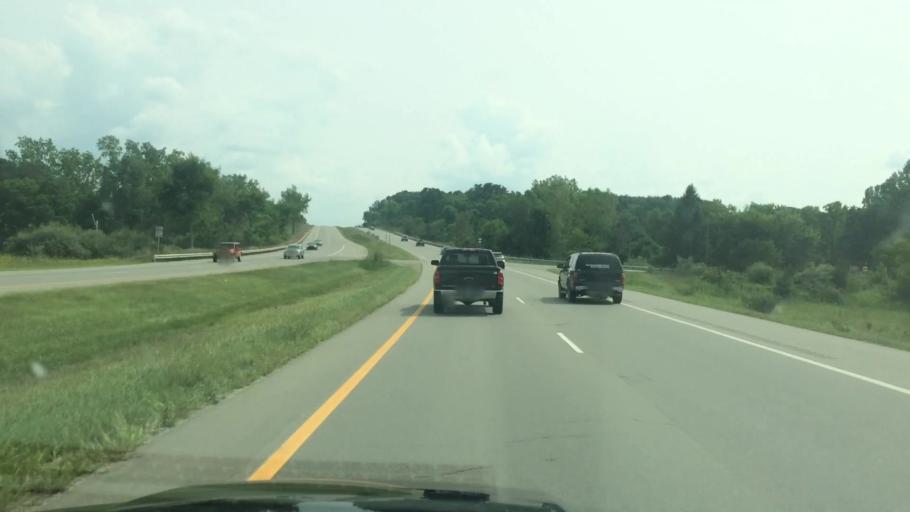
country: US
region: Michigan
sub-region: Oakland County
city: Oxford
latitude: 42.8920
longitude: -83.3111
